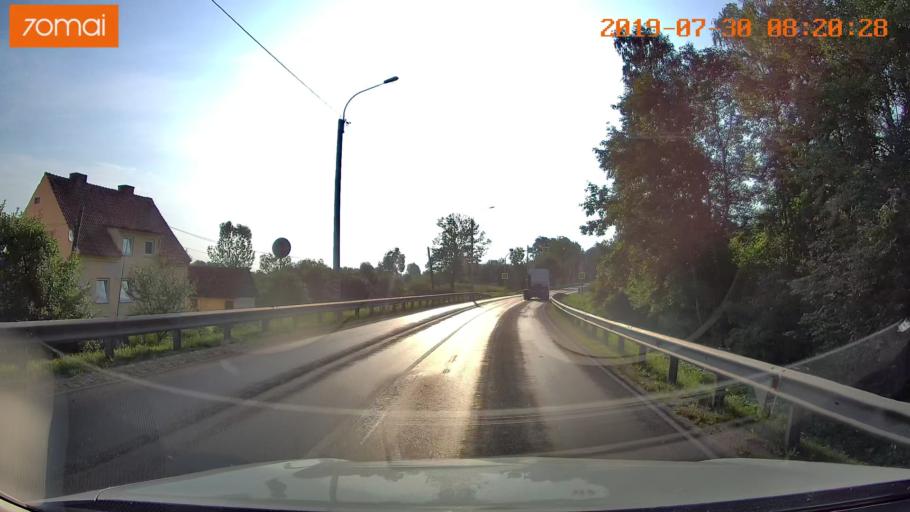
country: RU
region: Kaliningrad
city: Chernyakhovsk
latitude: 54.6267
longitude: 21.5160
